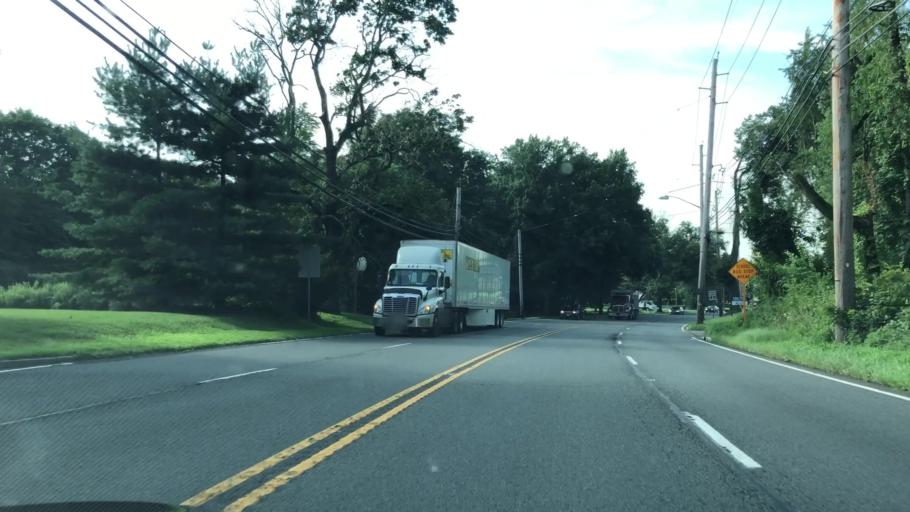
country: US
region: New Jersey
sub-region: Mercer County
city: Ewing
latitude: 40.2964
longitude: -74.7825
